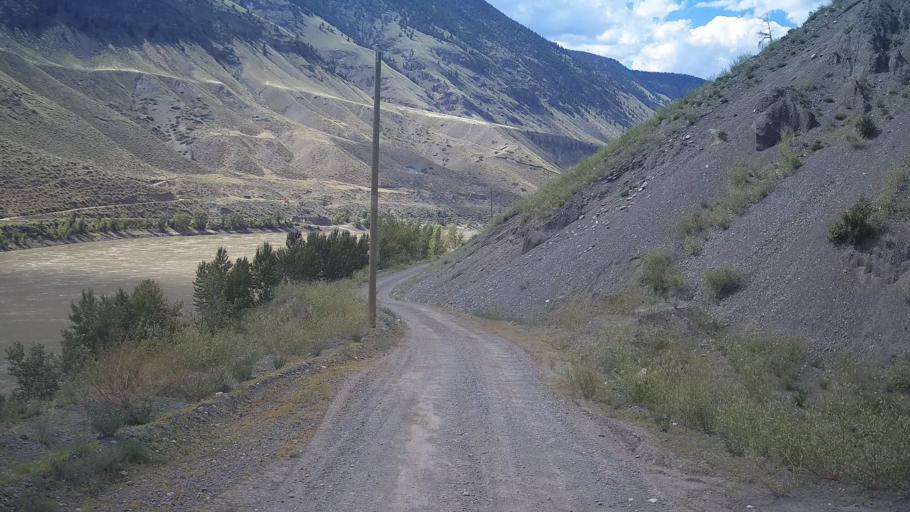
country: CA
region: British Columbia
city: Lillooet
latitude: 51.1821
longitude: -122.1256
